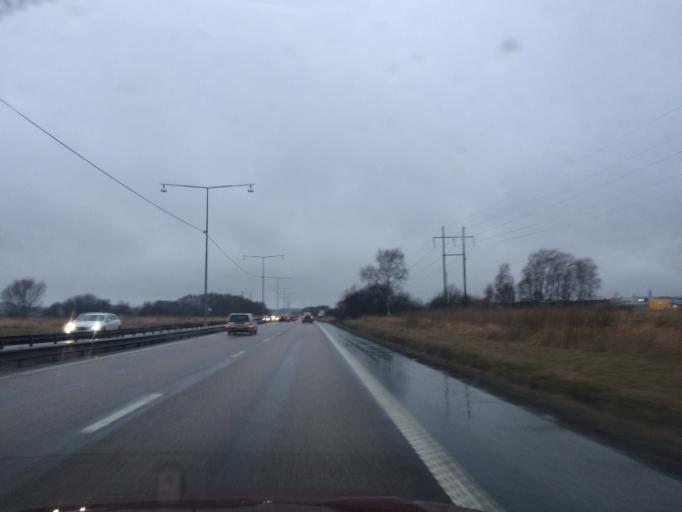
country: SE
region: Vaestra Goetaland
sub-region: Molndal
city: Moelndal
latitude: 57.6456
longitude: 11.9726
